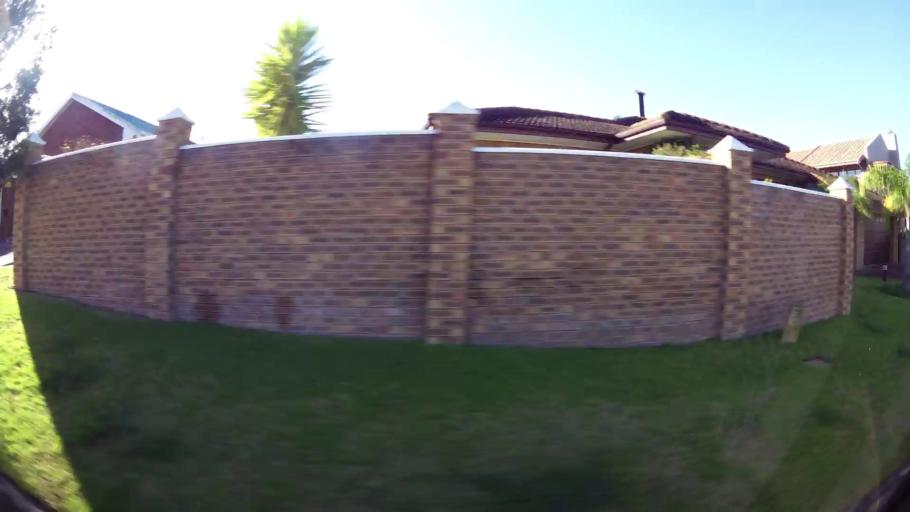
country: ZA
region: Western Cape
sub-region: Eden District Municipality
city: George
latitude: -33.9681
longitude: 22.4377
